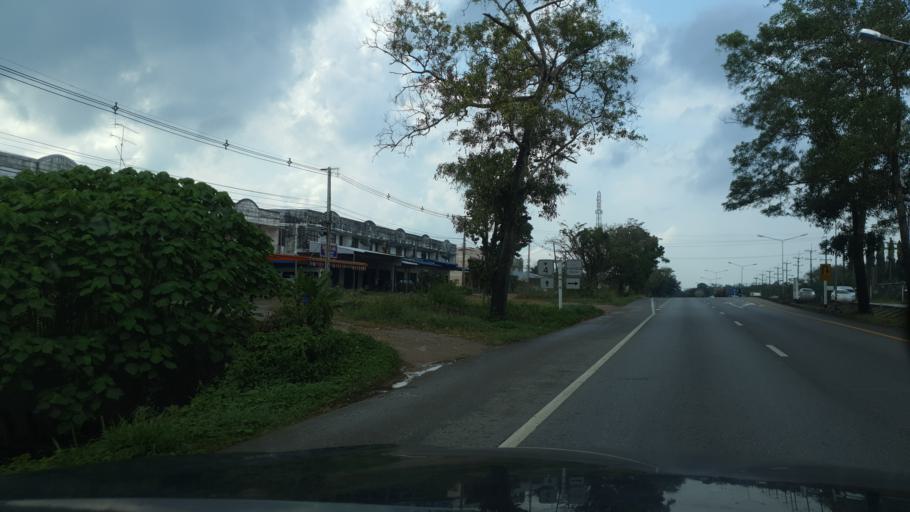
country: TH
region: Chumphon
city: Pathio
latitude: 10.9170
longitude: 99.2827
